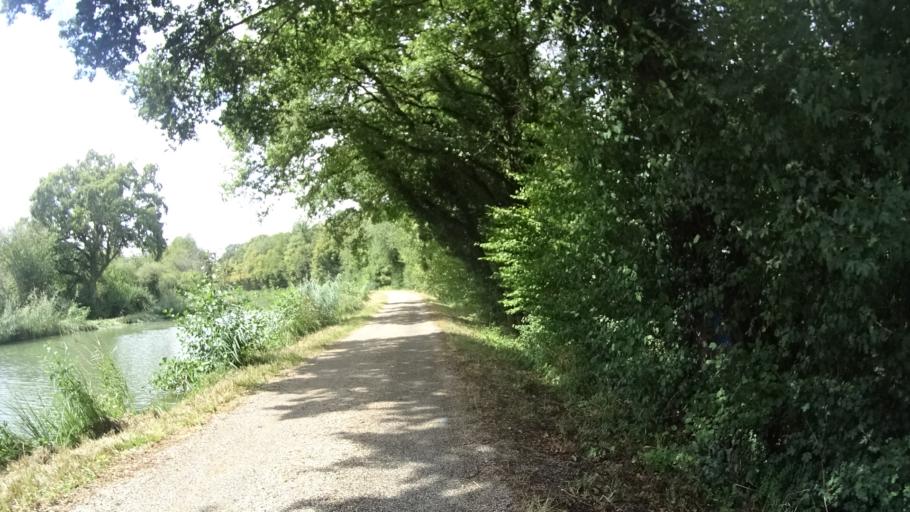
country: FR
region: Franche-Comte
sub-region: Departement du Jura
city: Saint-Aubin
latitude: 47.0877
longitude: 5.3365
